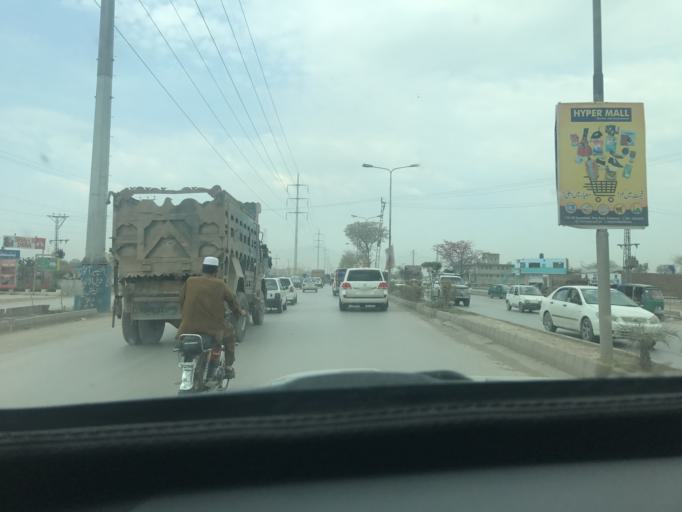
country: PK
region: Khyber Pakhtunkhwa
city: Peshawar
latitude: 33.9624
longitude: 71.5023
